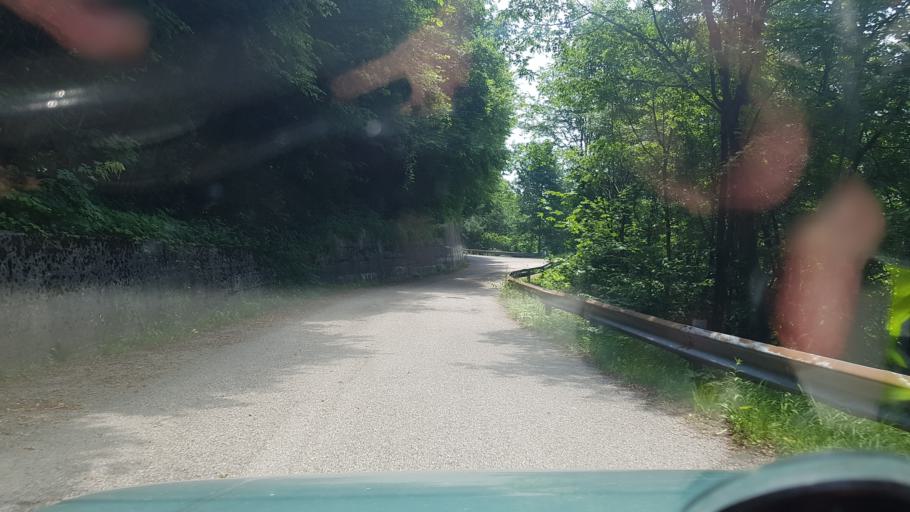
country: IT
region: Friuli Venezia Giulia
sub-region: Provincia di Udine
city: Lusevera
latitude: 46.2654
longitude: 13.2900
